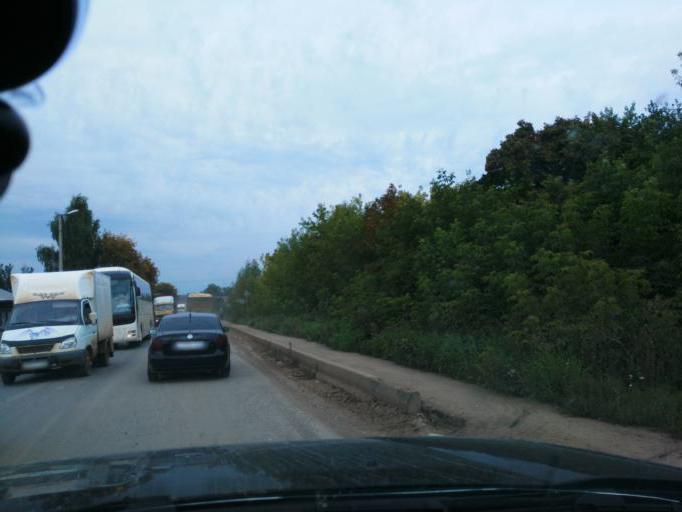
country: RU
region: Perm
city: Kuyeda
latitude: 56.4249
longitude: 55.5820
